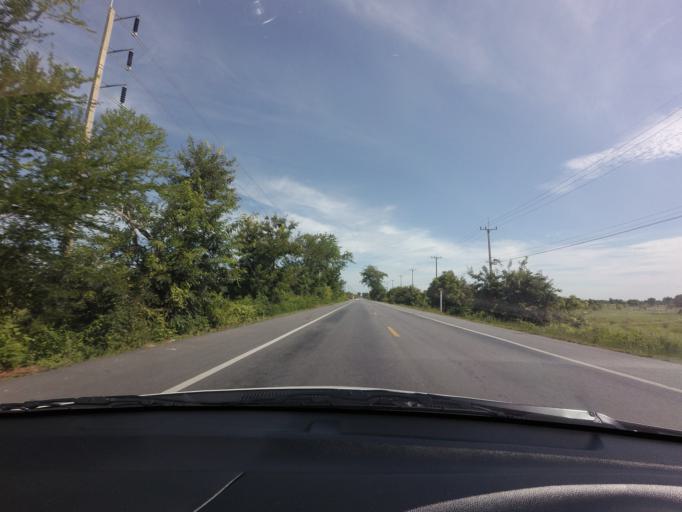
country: TH
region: Suphan Buri
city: Nong Yasai
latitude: 14.6871
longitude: 99.8476
